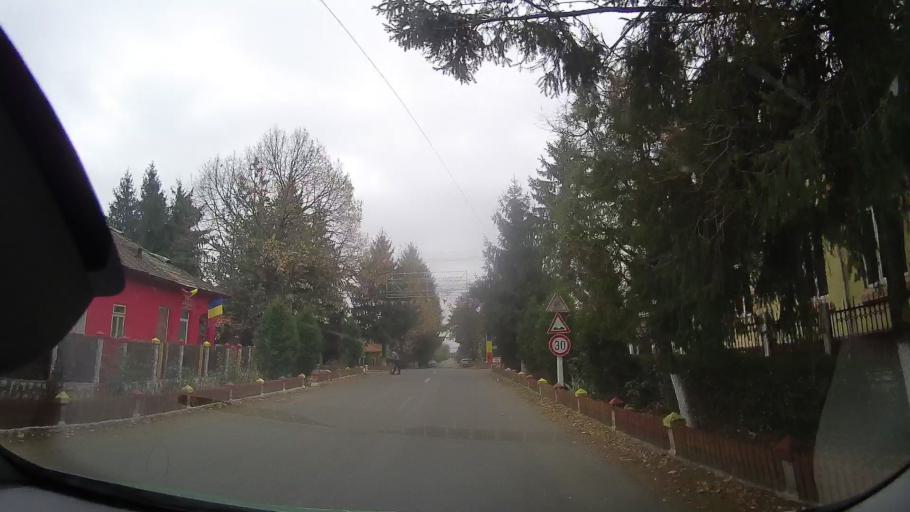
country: RO
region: Buzau
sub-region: Comuna Bradeanu
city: Bradeanu
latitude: 44.9259
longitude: 26.8613
